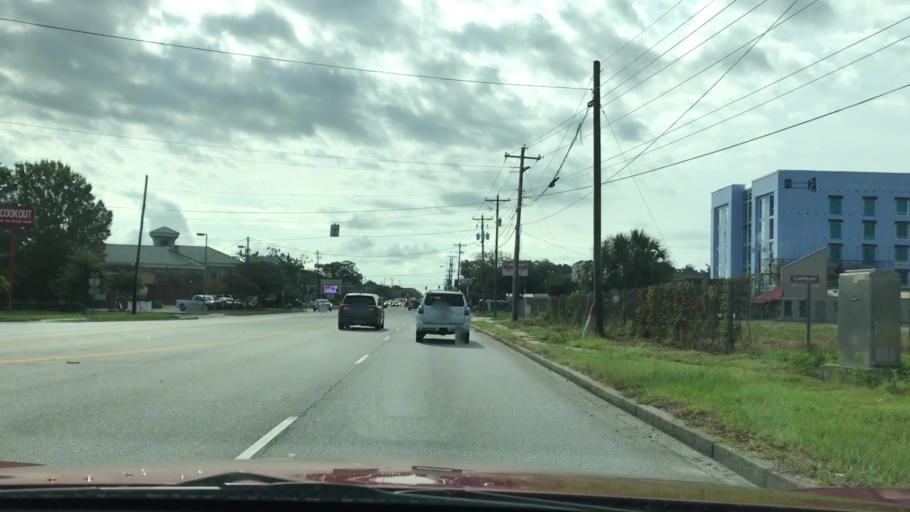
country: US
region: South Carolina
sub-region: Charleston County
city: Shell Point
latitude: 32.7897
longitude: -80.0302
